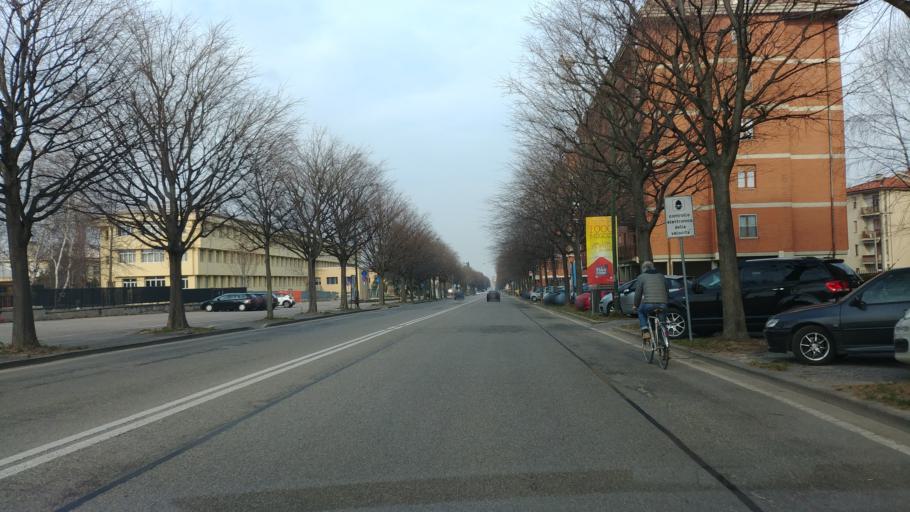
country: IT
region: Piedmont
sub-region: Provincia di Cuneo
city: Cuneo
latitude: 44.3766
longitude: 7.5266
